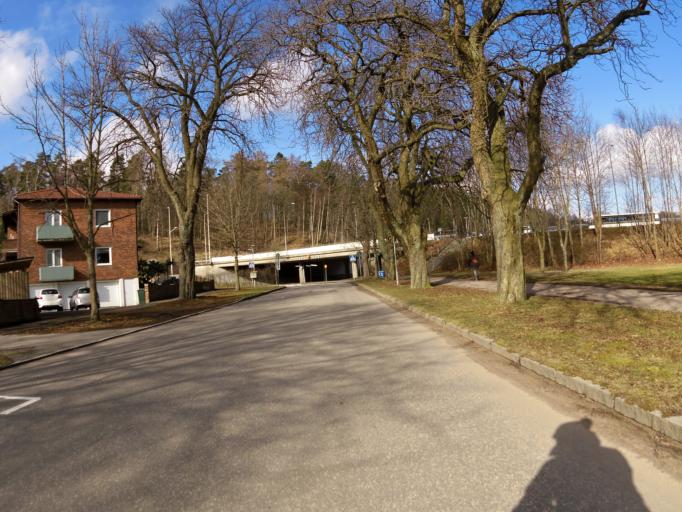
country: SE
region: Halland
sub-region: Halmstads Kommun
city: Halmstad
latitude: 56.6828
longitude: 12.8601
